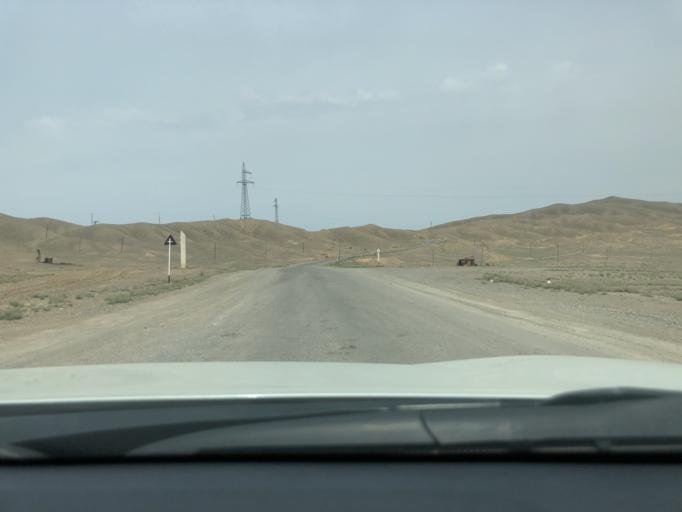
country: TJ
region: Viloyati Sughd
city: Kim
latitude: 40.2144
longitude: 70.4752
